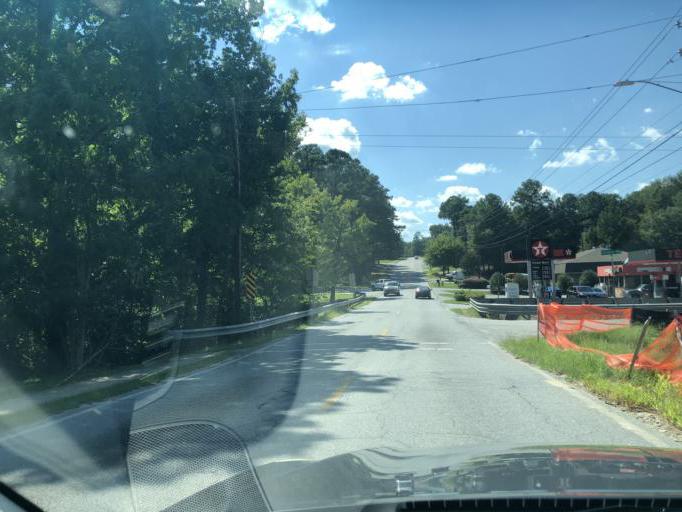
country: US
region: Georgia
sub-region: Muscogee County
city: Columbus
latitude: 32.5396
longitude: -84.9331
